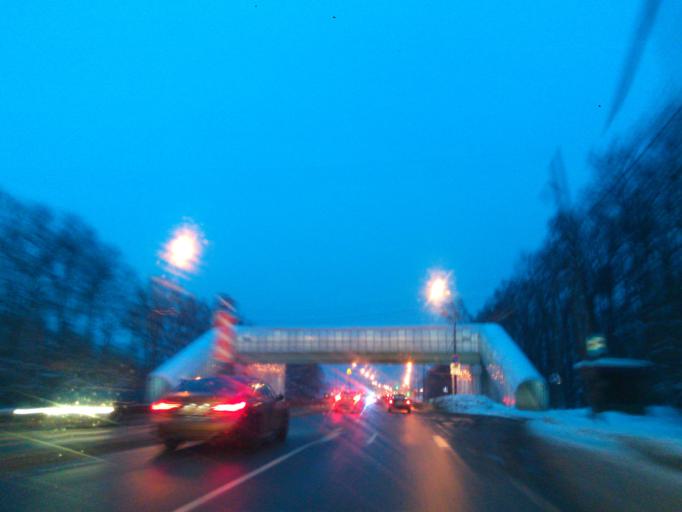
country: RU
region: Moskovskaya
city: Yermolino
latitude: 56.1510
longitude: 37.4880
